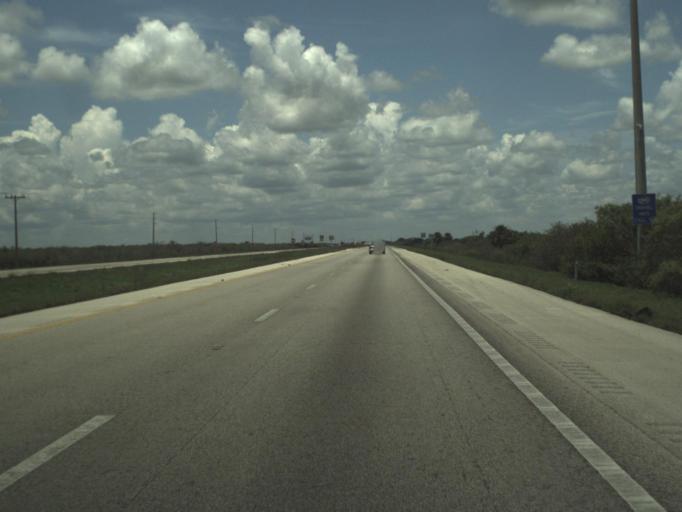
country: US
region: Florida
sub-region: Broward County
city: Weston
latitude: 26.1527
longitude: -80.7386
